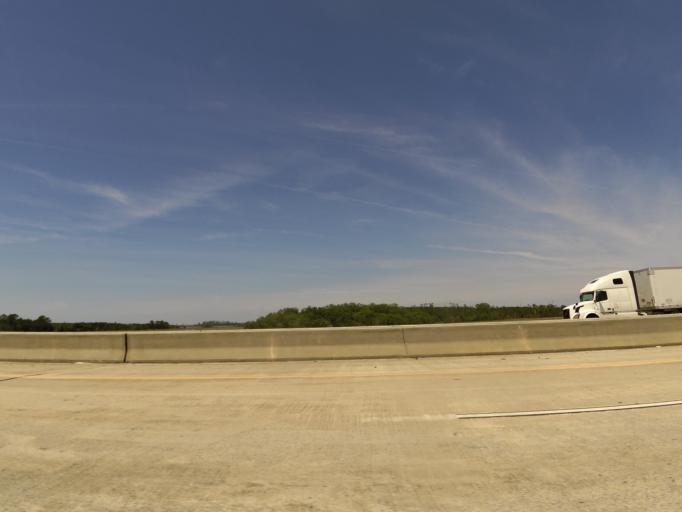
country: US
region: Georgia
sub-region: Glynn County
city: Dock Junction
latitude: 31.2085
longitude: -81.5336
